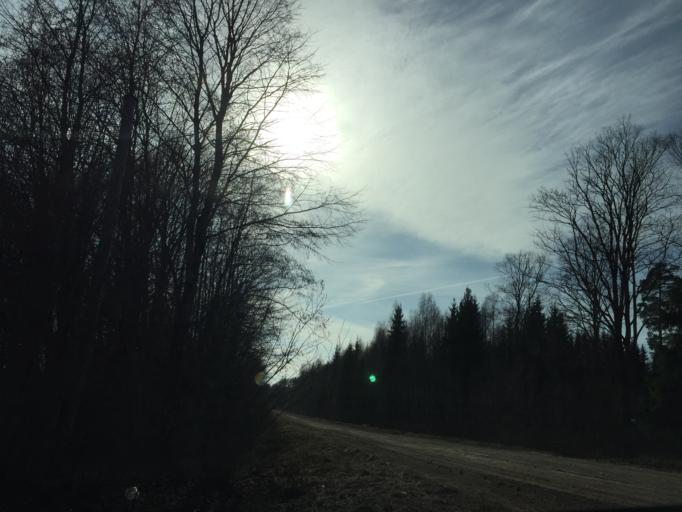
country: LV
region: Seja
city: Loja
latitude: 57.3075
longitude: 24.5802
